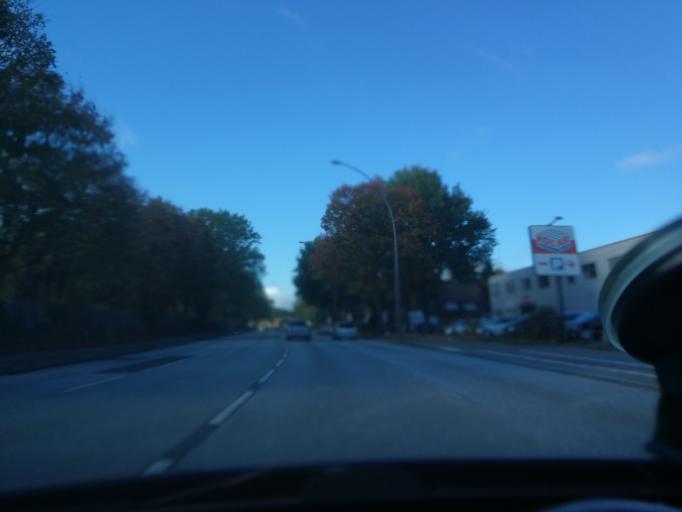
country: DE
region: Lower Saxony
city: Neu Wulmstorf
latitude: 53.4728
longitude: 9.8468
